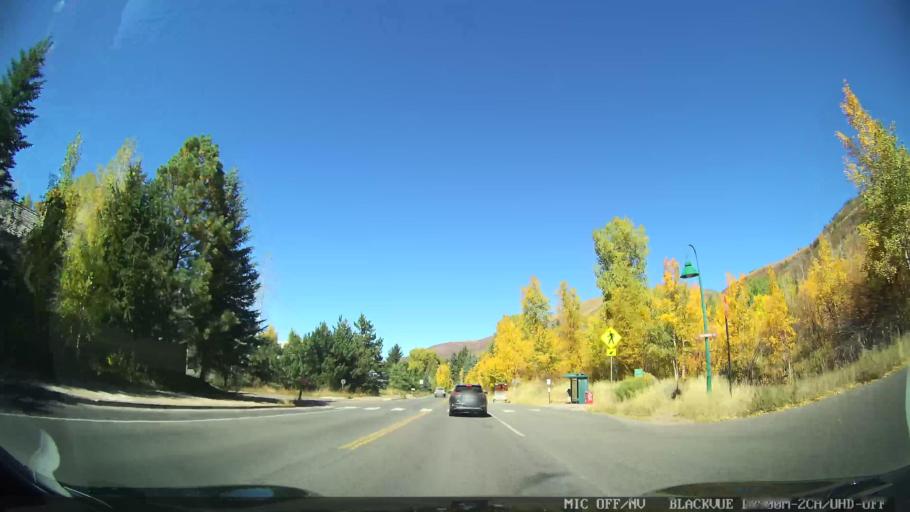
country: US
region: Colorado
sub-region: Pitkin County
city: Aspen
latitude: 39.1839
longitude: -106.8076
